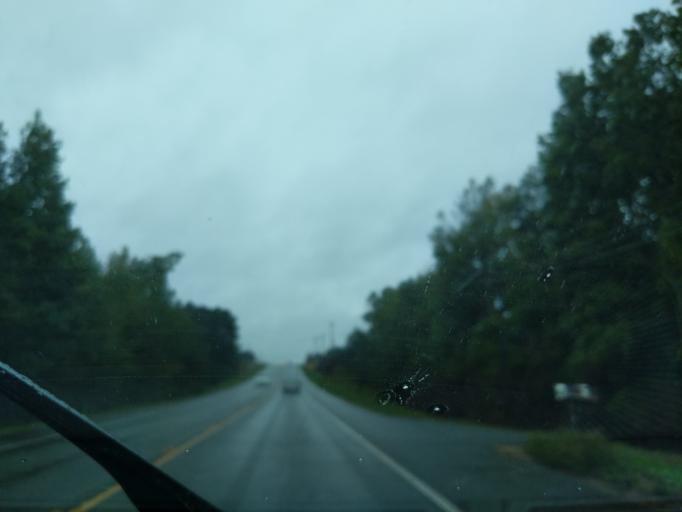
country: US
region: Louisiana
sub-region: Webster Parish
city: Minden
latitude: 32.6196
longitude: -93.2497
